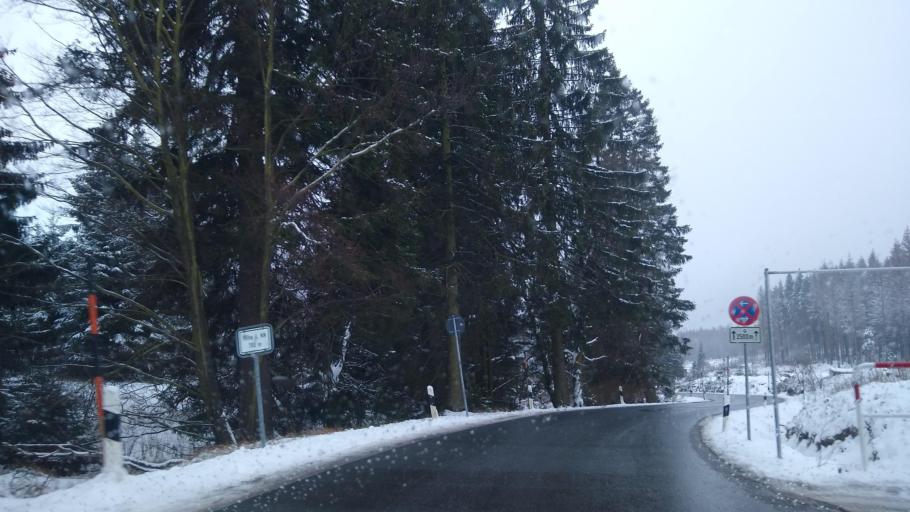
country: DE
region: Lower Saxony
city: Braunlage
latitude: 51.7496
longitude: 10.6311
